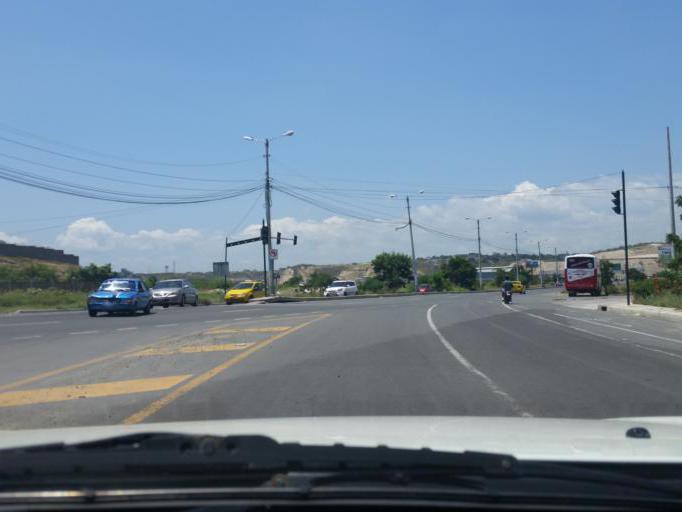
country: EC
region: Manabi
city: Manta
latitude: -0.9612
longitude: -80.7395
